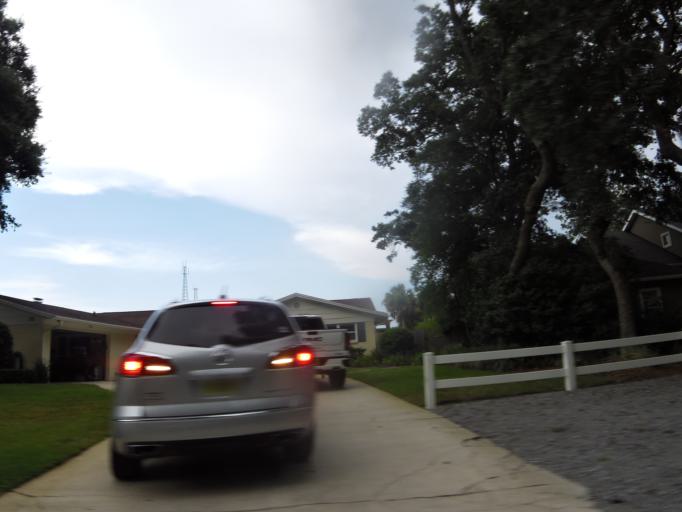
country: US
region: Florida
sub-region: Duval County
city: Jacksonville Beach
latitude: 30.2763
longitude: -81.4034
